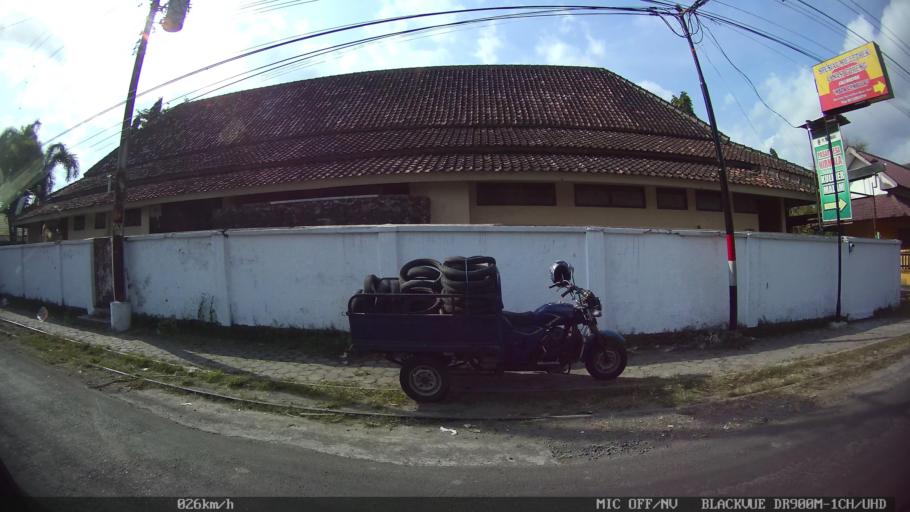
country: ID
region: Daerah Istimewa Yogyakarta
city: Kasihan
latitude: -7.8290
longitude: 110.3434
